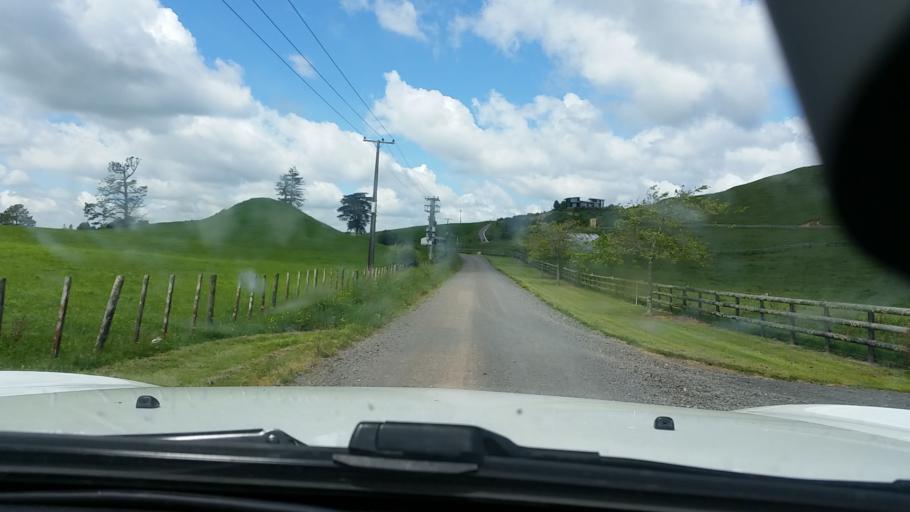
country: NZ
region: Bay of Plenty
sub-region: Rotorua District
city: Rotorua
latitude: -38.0248
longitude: 176.2807
